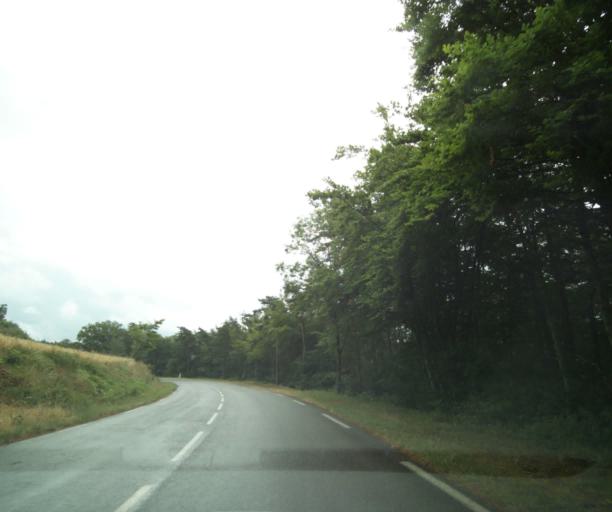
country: FR
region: Languedoc-Roussillon
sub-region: Departement de la Lozere
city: La Canourgue
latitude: 44.4096
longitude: 3.1507
